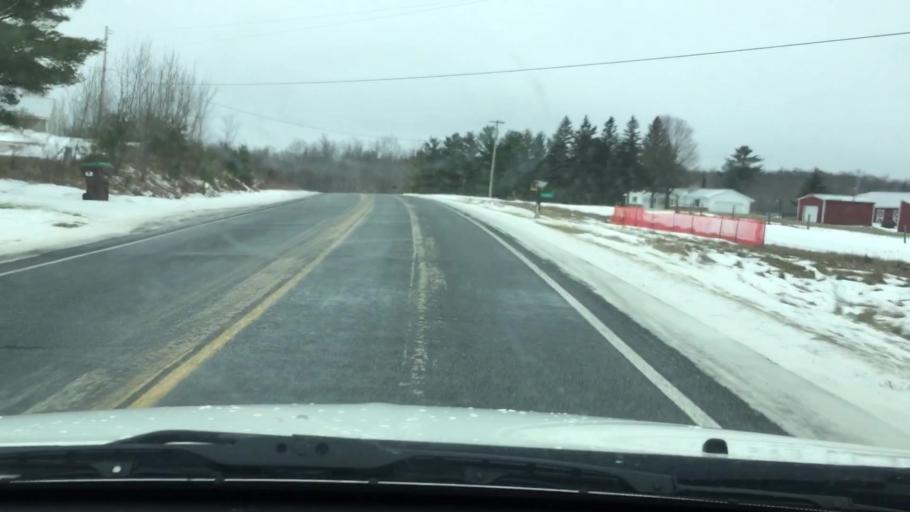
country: US
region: Michigan
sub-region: Wexford County
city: Cadillac
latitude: 44.1150
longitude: -85.4438
